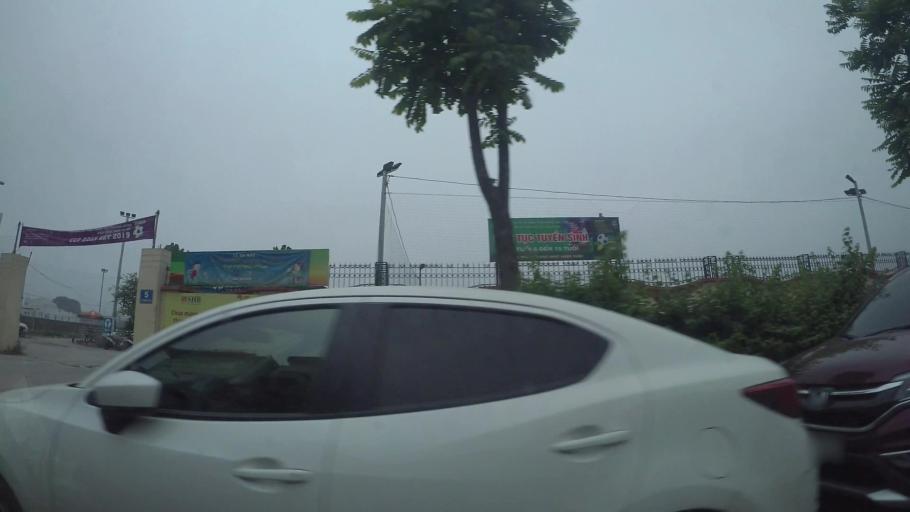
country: VN
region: Ha Noi
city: Hai BaTrung
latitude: 20.9940
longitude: 105.8315
